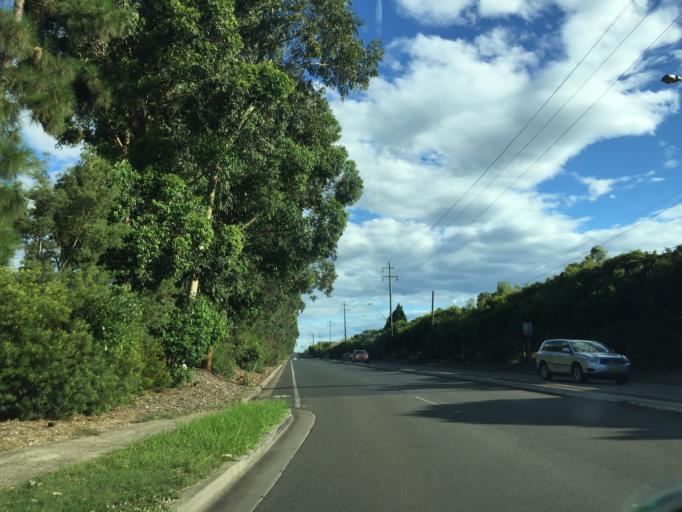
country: AU
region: New South Wales
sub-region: The Hills Shire
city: Glenhaven
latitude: -33.7014
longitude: 150.9706
